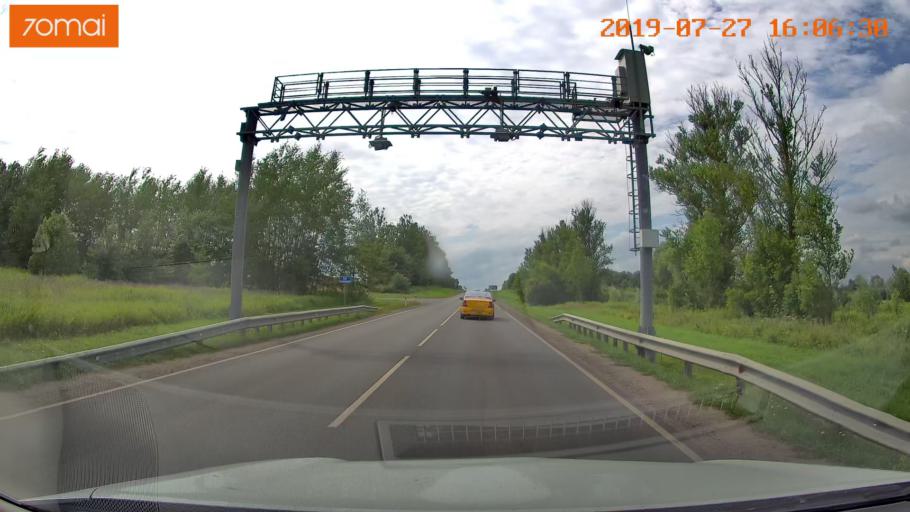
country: RU
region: Kaliningrad
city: Chernyakhovsk
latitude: 54.6340
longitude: 21.7761
